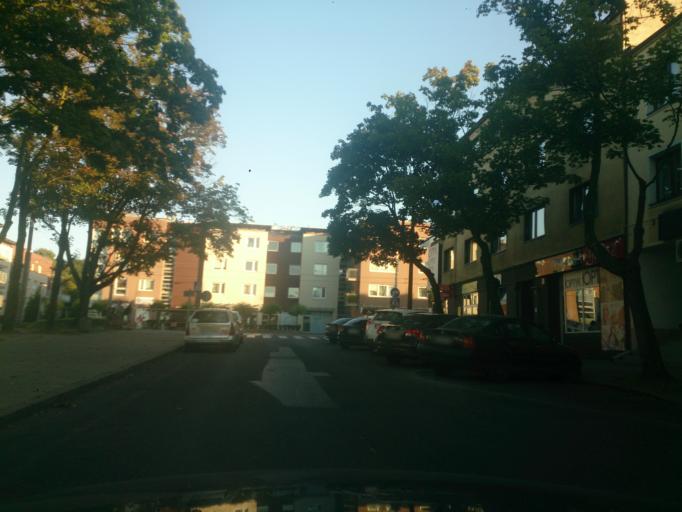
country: PL
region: Pomeranian Voivodeship
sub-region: Gdynia
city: Gdynia
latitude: 54.4838
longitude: 18.5379
